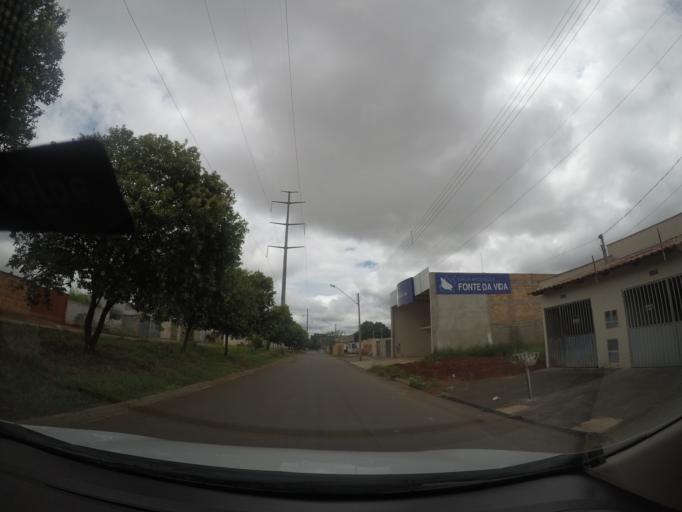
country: BR
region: Goias
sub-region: Goiania
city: Goiania
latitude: -16.7312
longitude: -49.3585
